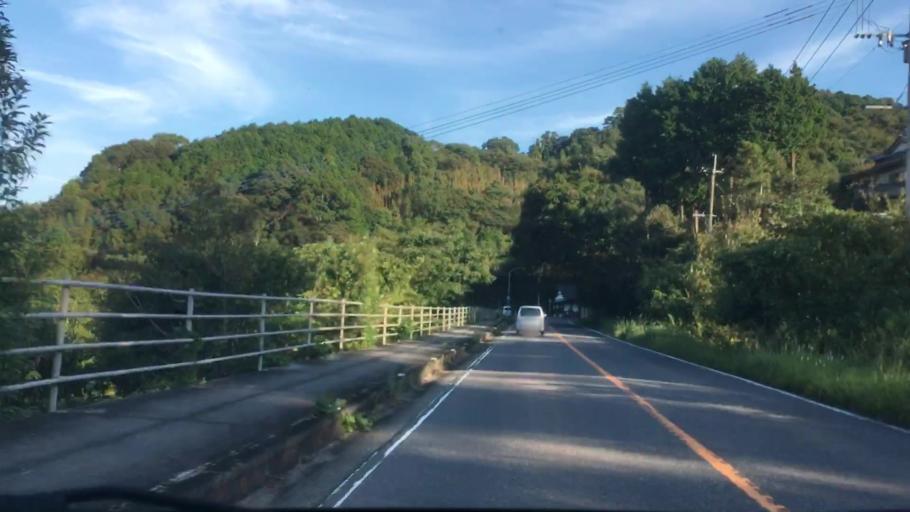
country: JP
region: Nagasaki
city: Sasebo
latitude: 33.0451
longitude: 129.7295
